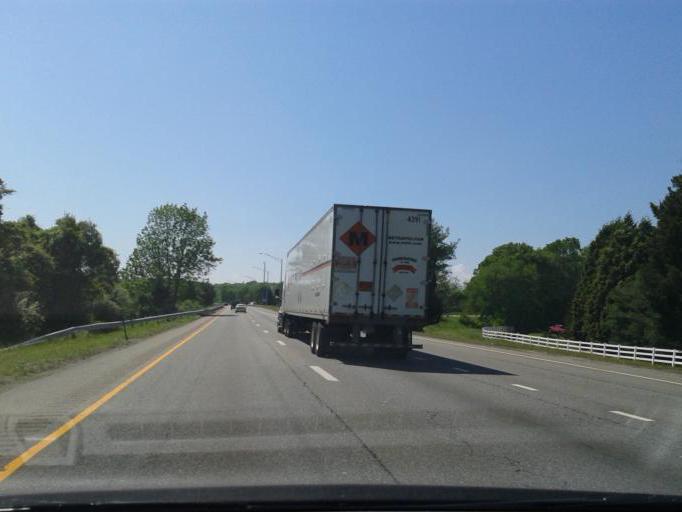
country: US
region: Connecticut
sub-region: New London County
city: Old Mystic
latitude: 41.3750
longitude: -71.9526
